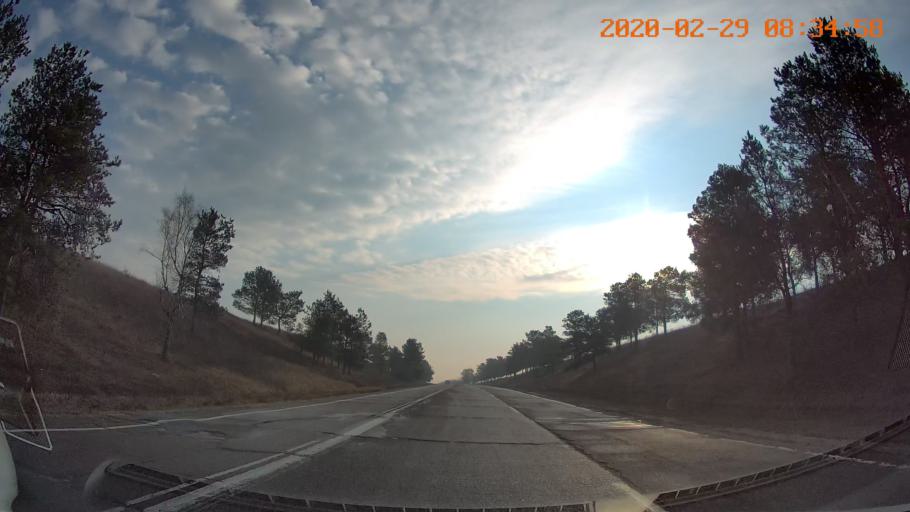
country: MD
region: Anenii Noi
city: Anenii Noi
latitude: 46.9234
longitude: 29.3193
